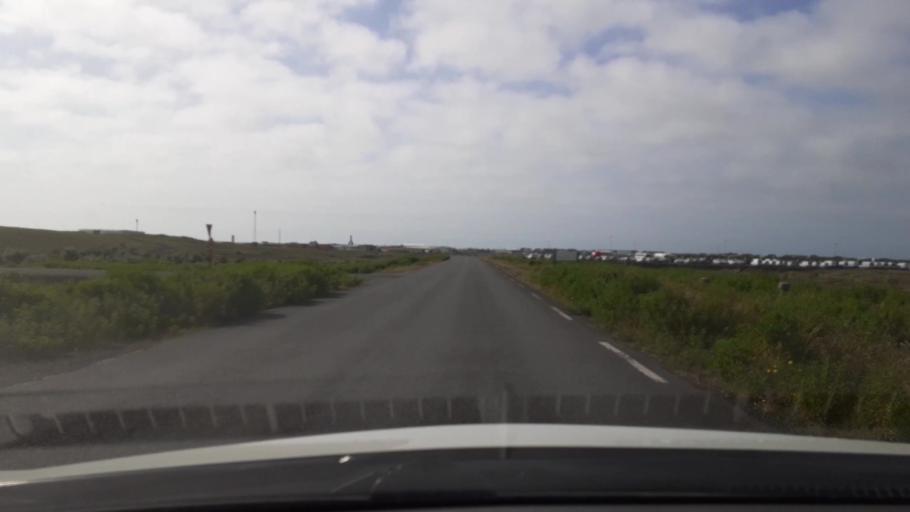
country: IS
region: South
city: THorlakshoefn
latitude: 63.8682
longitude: -21.3826
